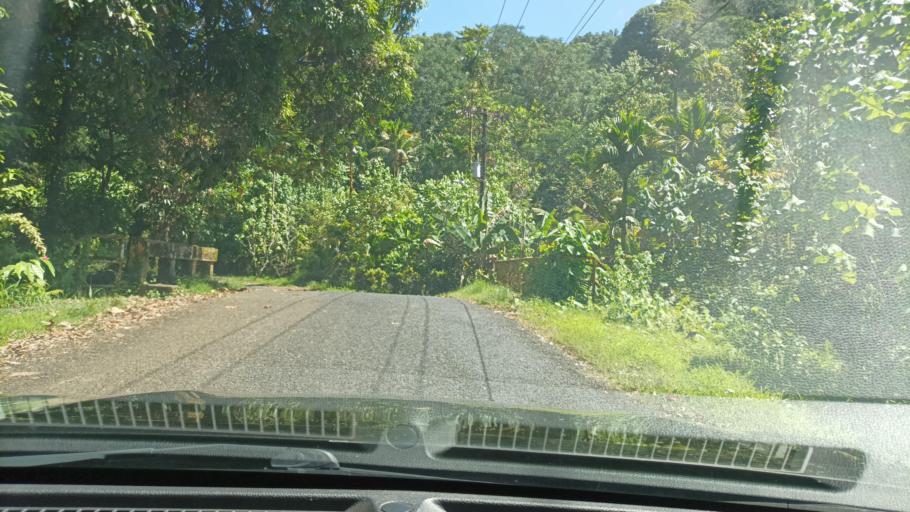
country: FM
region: Pohnpei
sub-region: Madolenihm Municipality
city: Madolenihm Municipality Government
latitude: 6.8590
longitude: 158.2916
